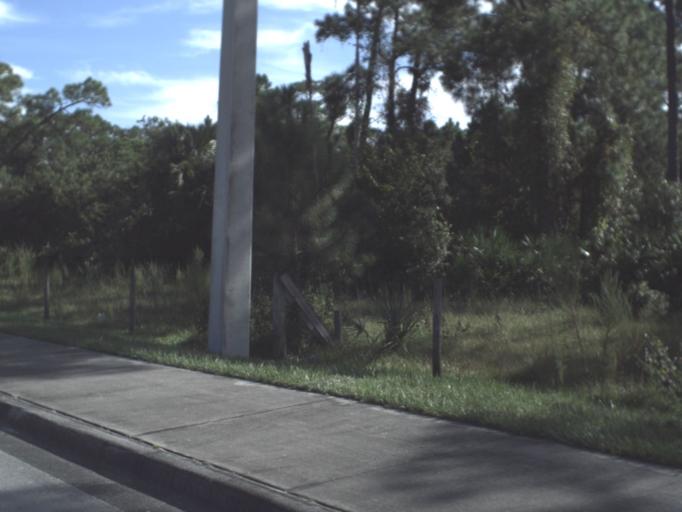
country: US
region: Florida
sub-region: Okeechobee County
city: Cypress Quarters
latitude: 27.2728
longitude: -80.8297
